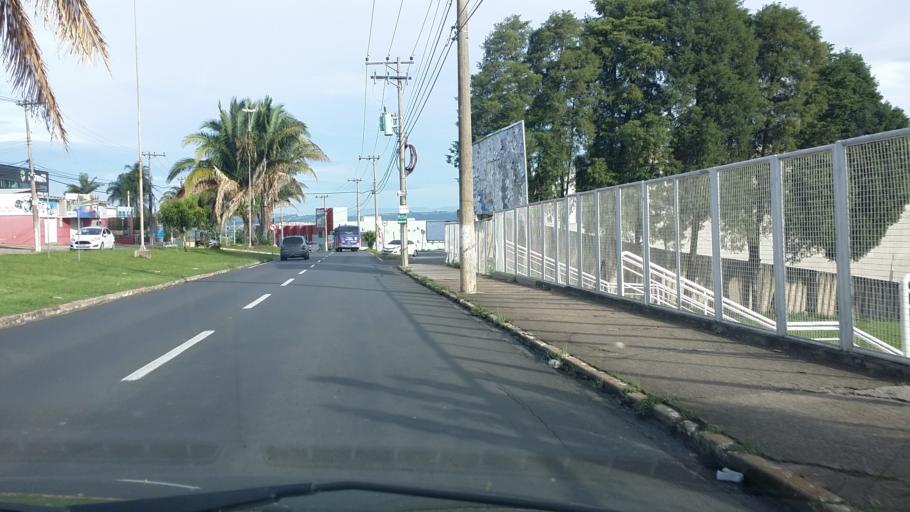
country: BR
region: Sao Paulo
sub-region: Indaiatuba
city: Indaiatuba
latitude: -23.0928
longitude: -47.1940
